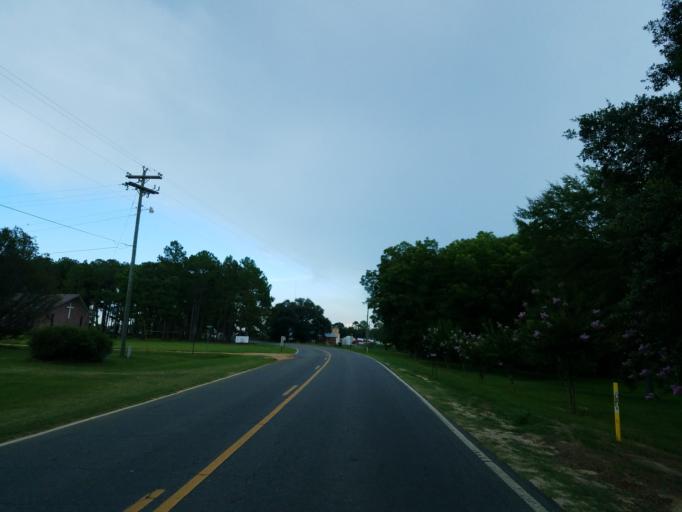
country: US
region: Georgia
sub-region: Cook County
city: Sparks
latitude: 31.2658
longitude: -83.4775
